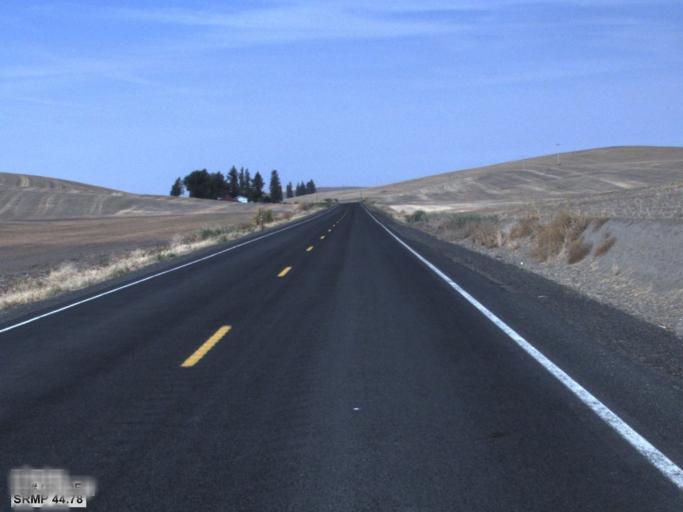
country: US
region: Idaho
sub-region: Benewah County
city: Plummer
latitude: 47.1946
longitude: -117.1206
